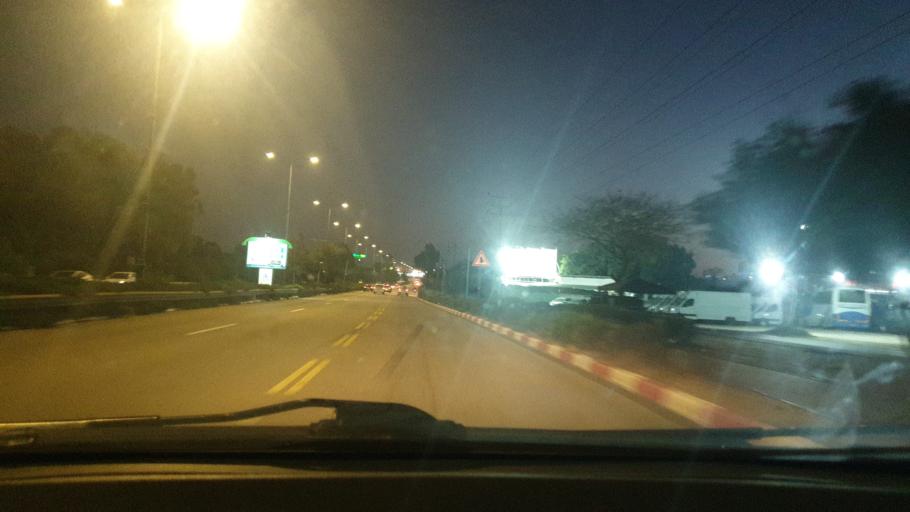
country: IL
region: Central District
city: Bet Dagan
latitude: 31.9906
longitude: 34.8123
